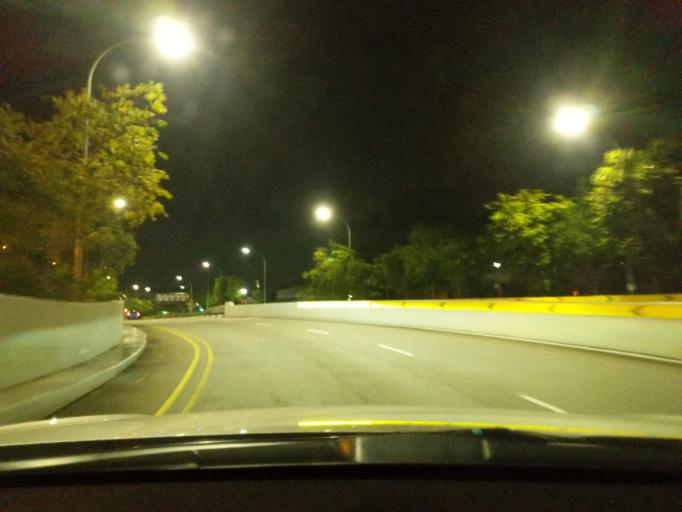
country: SG
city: Singapore
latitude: 1.3046
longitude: 103.8698
